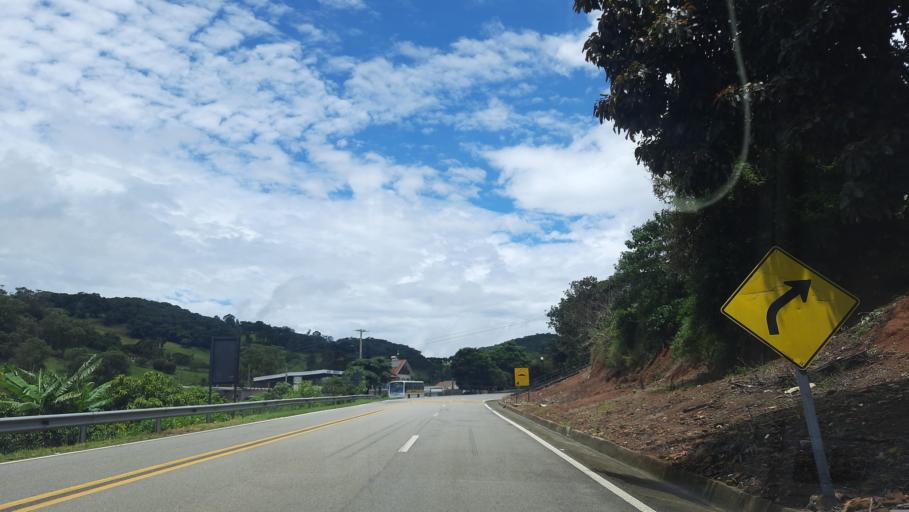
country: BR
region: Sao Paulo
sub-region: Sao Joao Da Boa Vista
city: Sao Joao da Boa Vista
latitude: -21.8353
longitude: -46.7456
